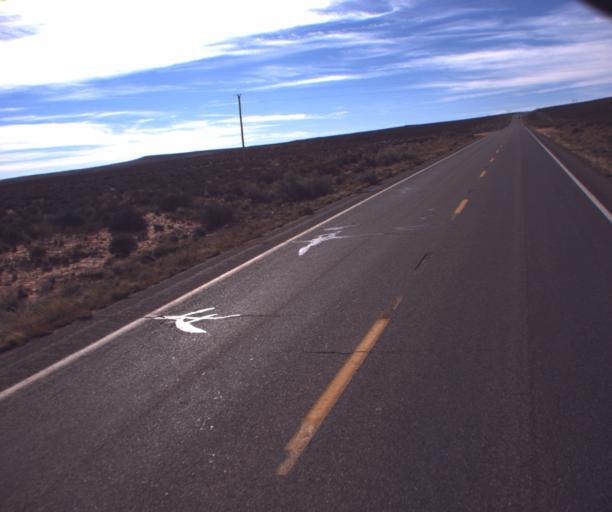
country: US
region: Arizona
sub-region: Coconino County
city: LeChee
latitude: 36.8216
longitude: -111.3082
